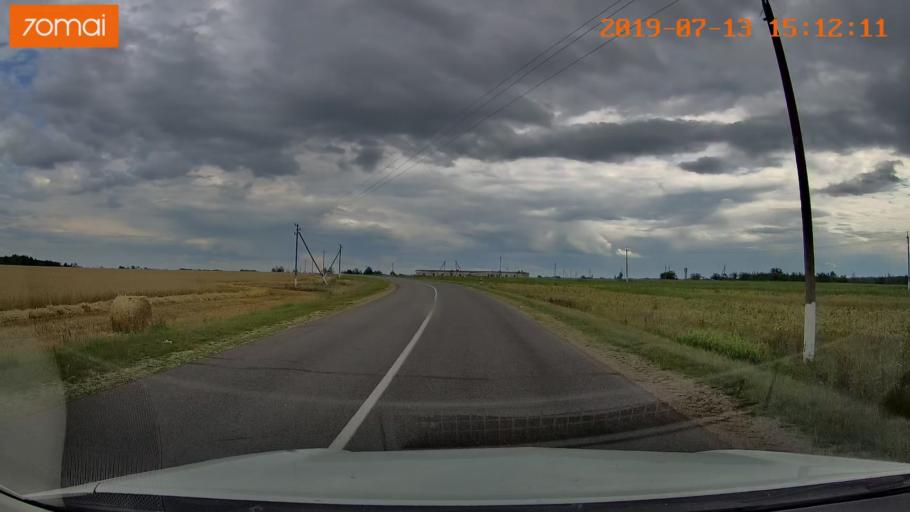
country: BY
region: Mogilev
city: Hlusha
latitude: 53.1519
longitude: 28.7882
